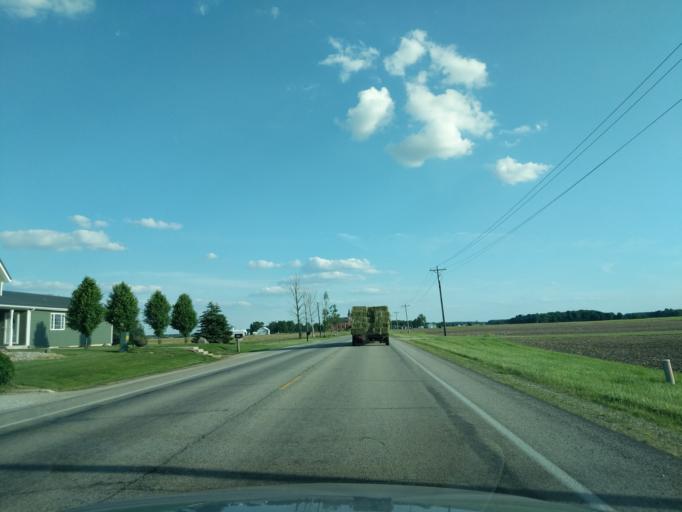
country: US
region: Indiana
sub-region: Huntington County
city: Roanoke
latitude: 41.0245
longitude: -85.4707
